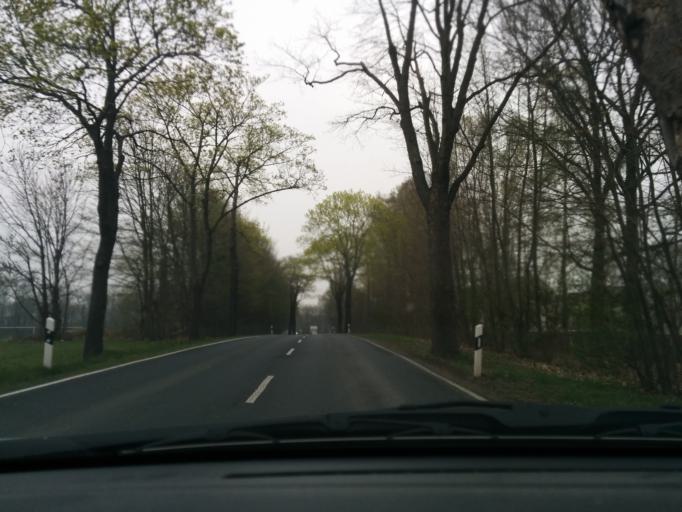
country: DE
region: Saxony
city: Oederan
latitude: 50.8658
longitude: 13.1812
